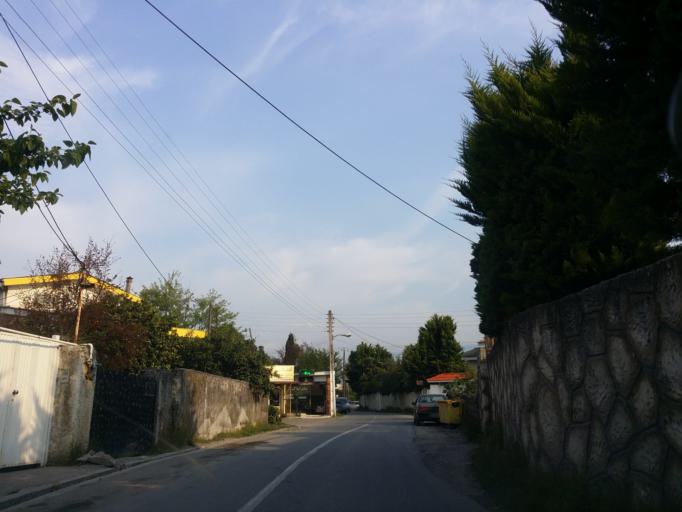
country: IR
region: Mazandaran
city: Chalus
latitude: 36.6873
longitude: 51.3714
